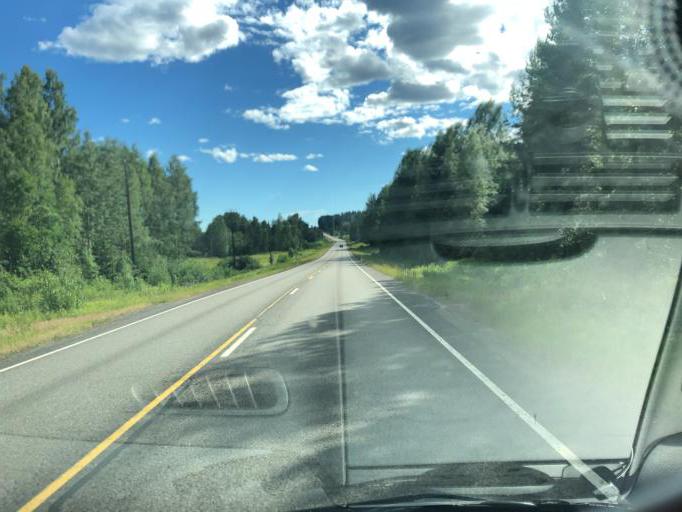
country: FI
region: Kymenlaakso
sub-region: Kouvola
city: Kouvola
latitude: 60.9853
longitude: 26.9146
